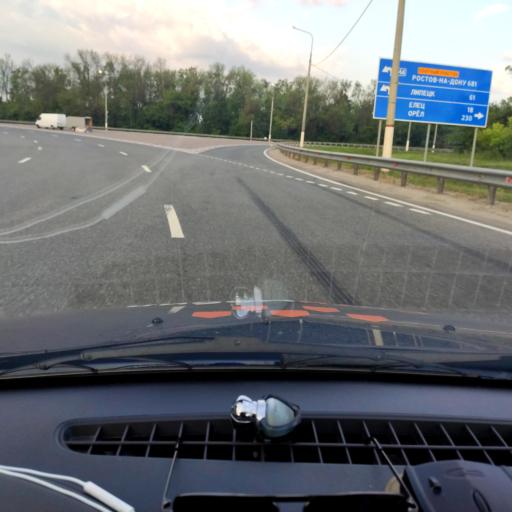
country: RU
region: Lipetsk
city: Yelets
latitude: 52.5489
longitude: 38.7154
